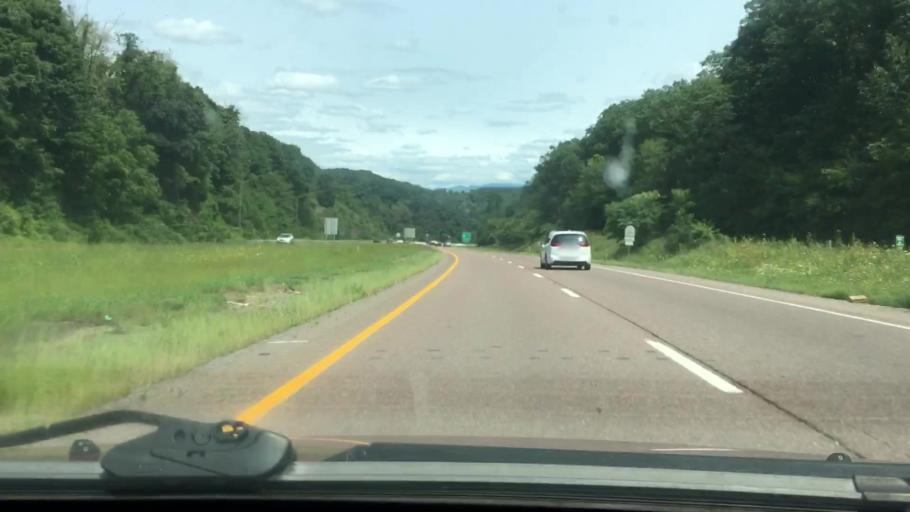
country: US
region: Maryland
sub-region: Allegany County
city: Cumberland
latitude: 39.6685
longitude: -78.7346
